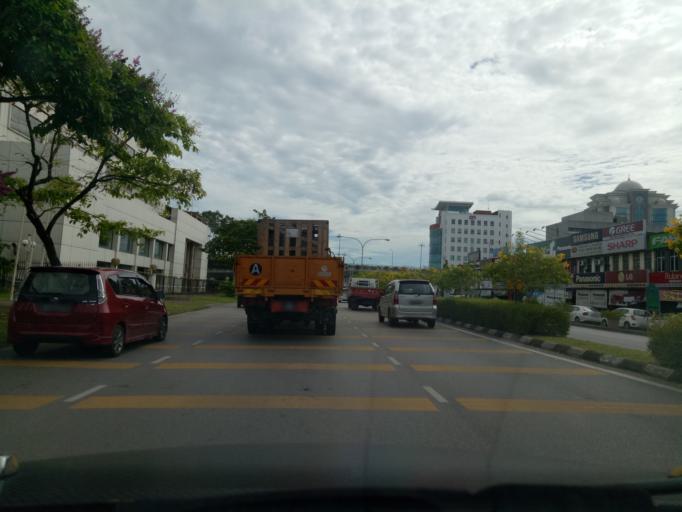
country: MY
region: Sarawak
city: Kuching
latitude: 1.5520
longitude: 110.3378
